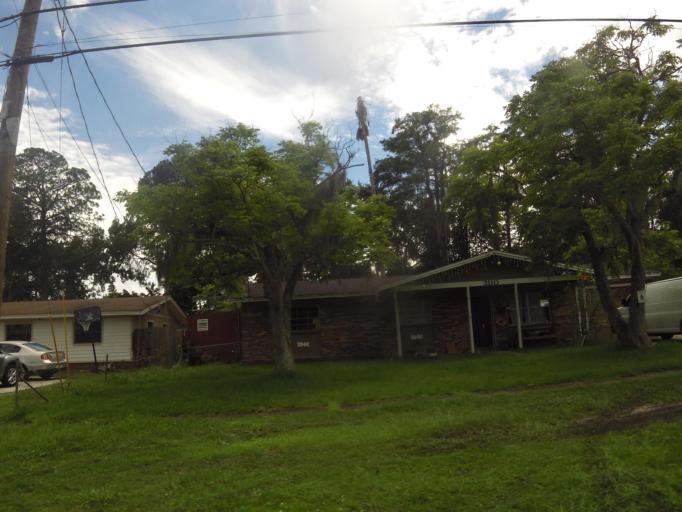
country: US
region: Florida
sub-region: Duval County
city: Jacksonville
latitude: 30.2687
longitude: -81.6069
